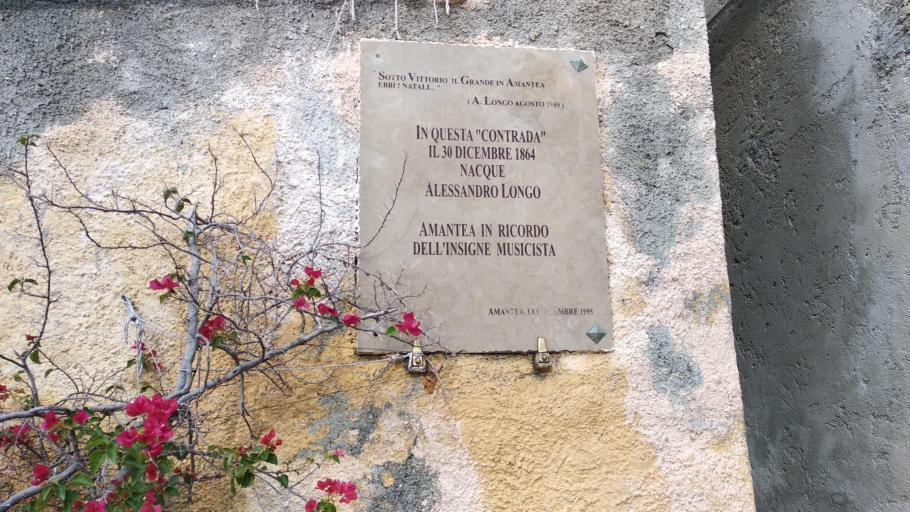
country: IT
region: Calabria
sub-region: Provincia di Cosenza
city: Amantea
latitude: 39.1367
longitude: 16.0735
